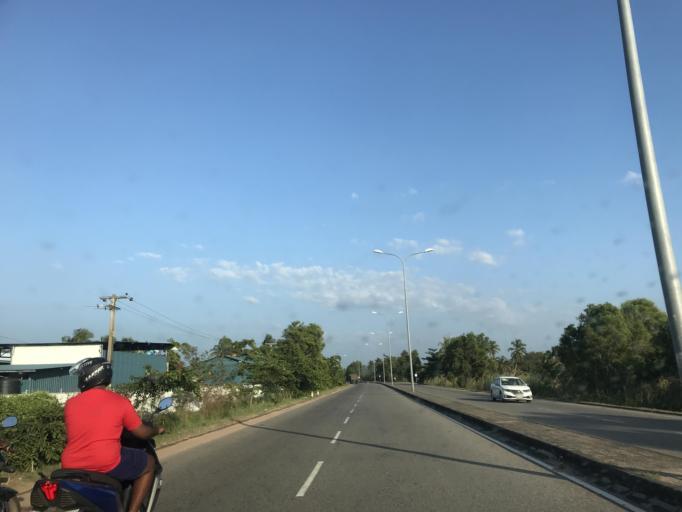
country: LK
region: Western
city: Ja Ela
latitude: 7.0814
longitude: 79.8812
